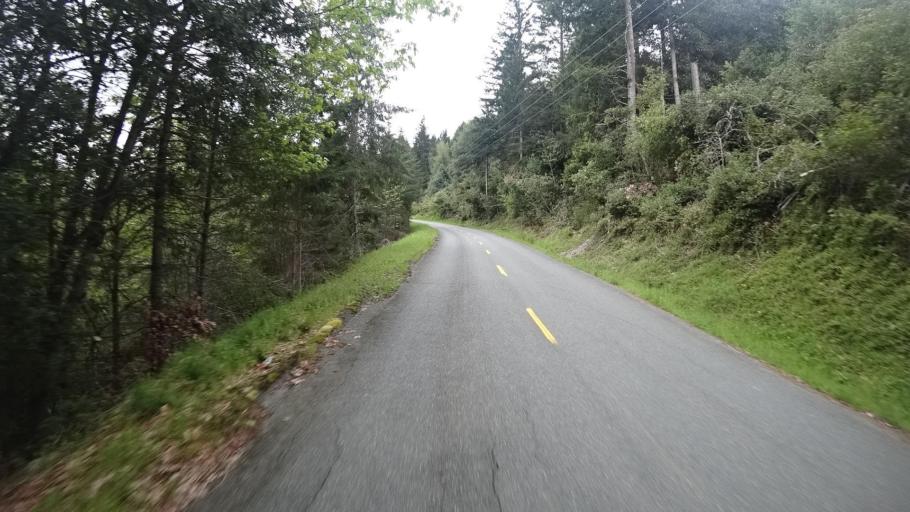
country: US
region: California
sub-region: Humboldt County
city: Blue Lake
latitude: 40.9320
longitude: -123.8452
